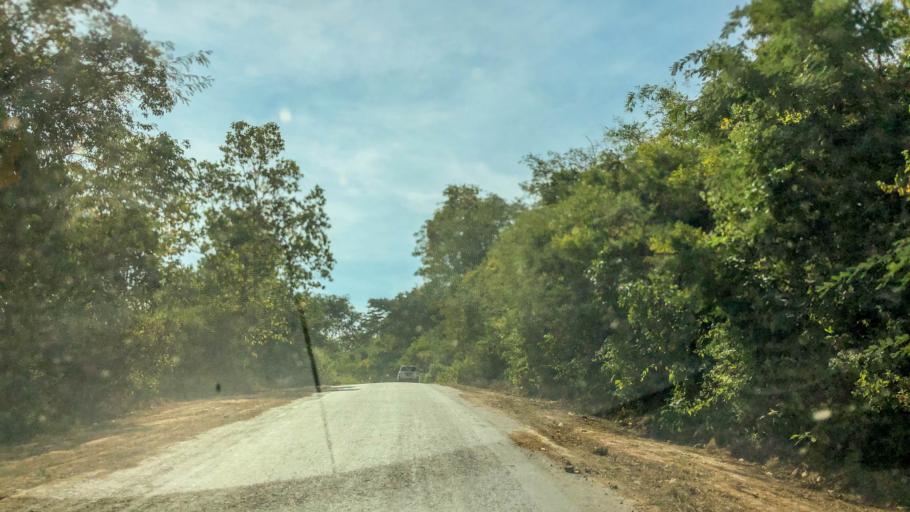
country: MM
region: Magway
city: Magway
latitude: 19.7633
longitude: 94.9379
